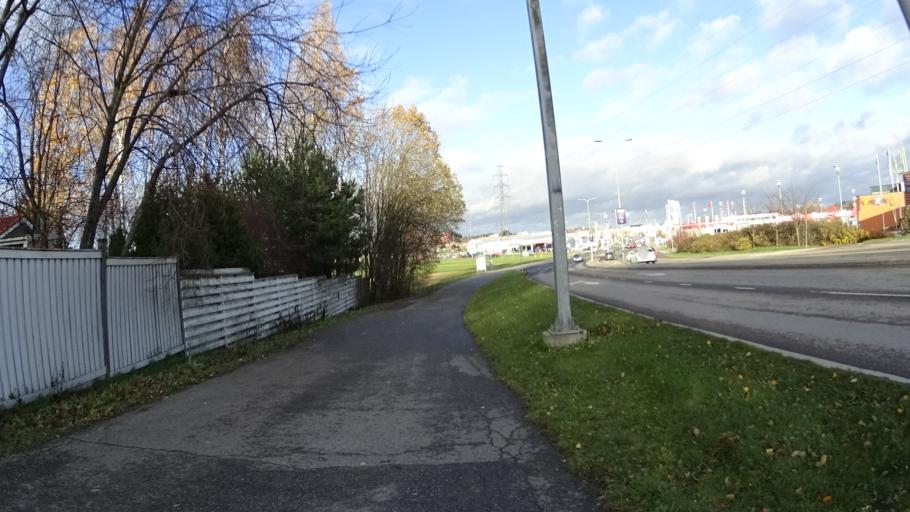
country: FI
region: Uusimaa
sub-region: Helsinki
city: Vantaa
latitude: 60.2783
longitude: 24.9703
